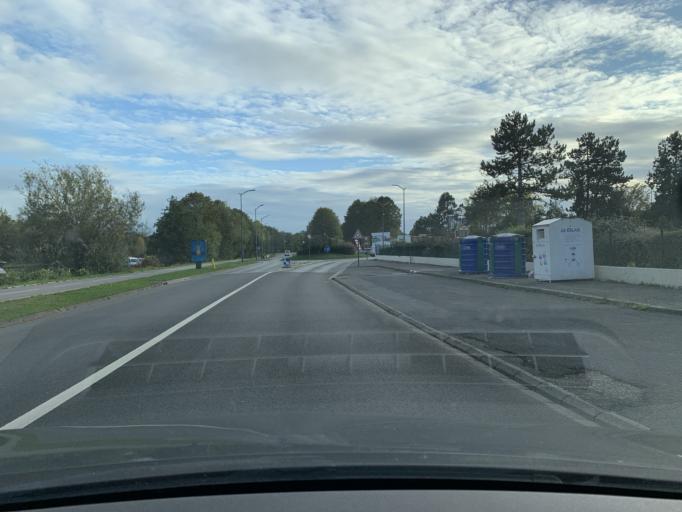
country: FR
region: Picardie
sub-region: Departement de l'Aisne
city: Harly
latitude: 49.8551
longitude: 3.3105
